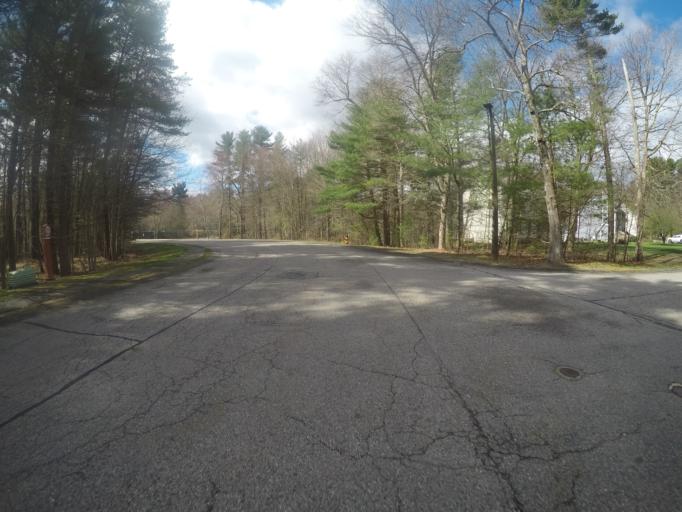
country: US
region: Massachusetts
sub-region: Bristol County
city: Easton
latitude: 42.0409
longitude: -71.1306
